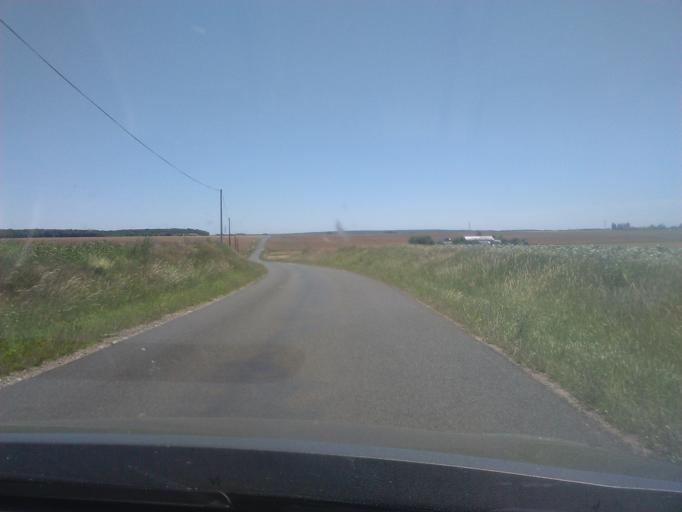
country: FR
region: Centre
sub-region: Departement du Loir-et-Cher
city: Herbault
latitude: 47.6438
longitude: 1.1933
